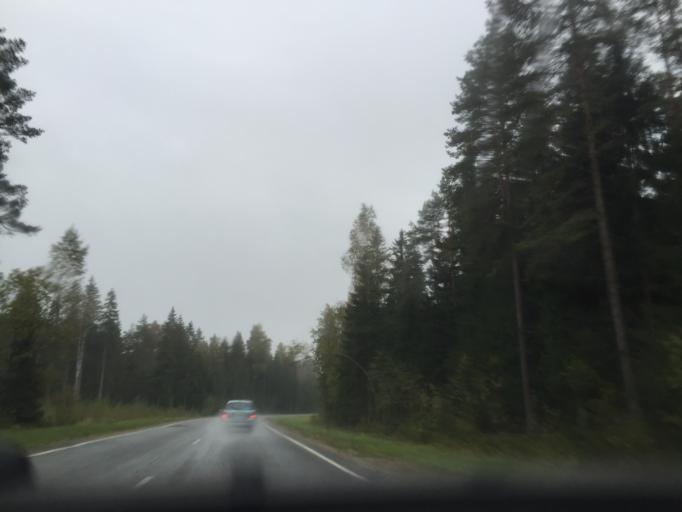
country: LV
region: Incukalns
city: Incukalns
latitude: 57.0563
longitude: 24.6714
